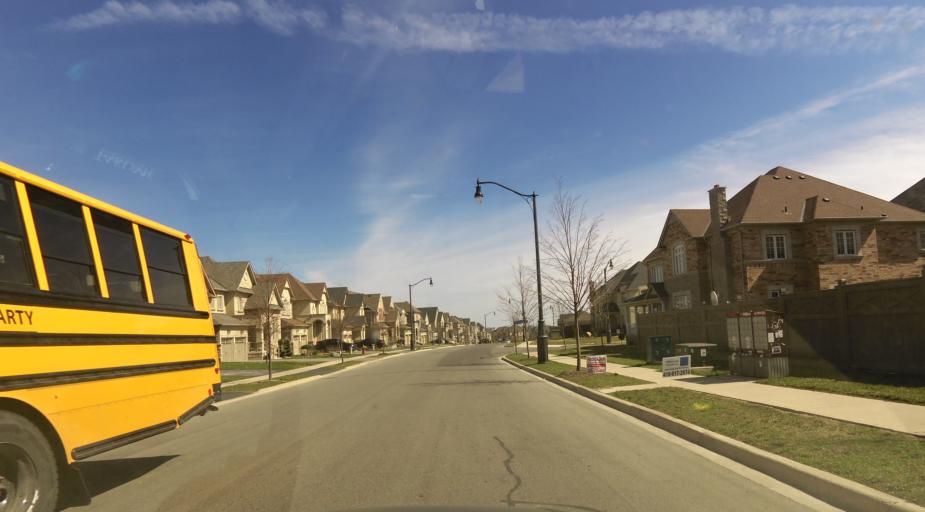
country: CA
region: Ontario
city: Brampton
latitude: 43.6542
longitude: -79.8088
